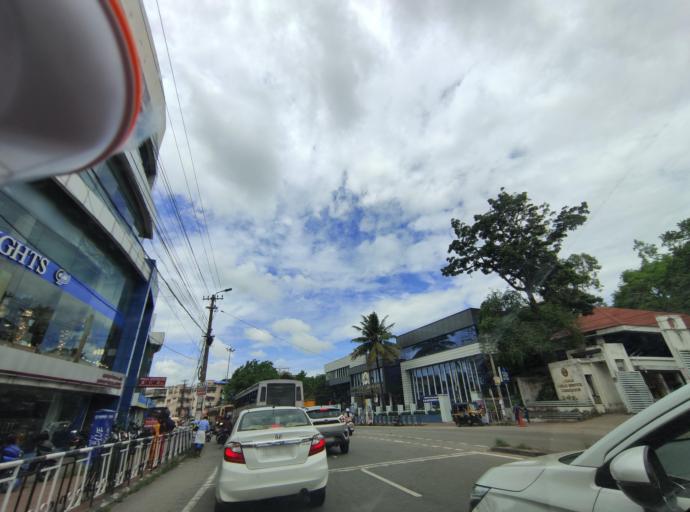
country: IN
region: Kerala
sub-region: Thiruvananthapuram
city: Thiruvananthapuram
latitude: 8.5196
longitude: 76.9419
